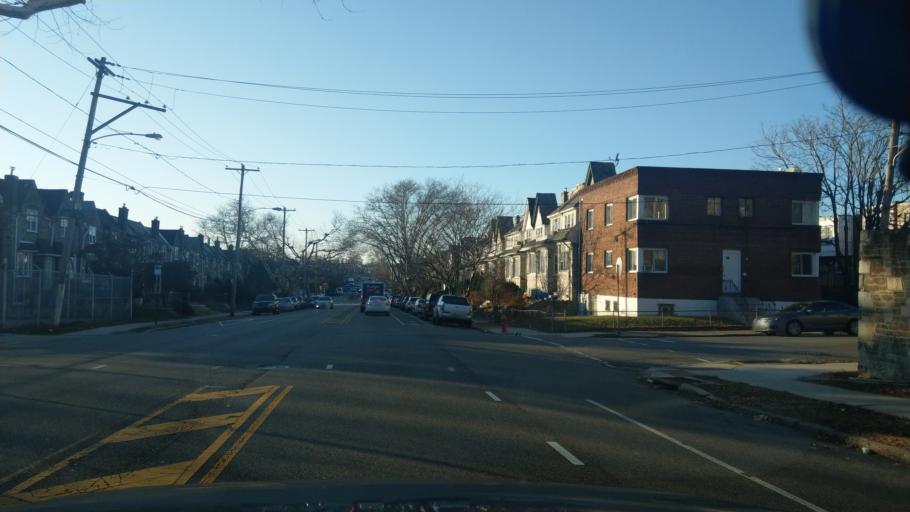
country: US
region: Pennsylvania
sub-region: Montgomery County
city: Wyncote
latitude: 40.0538
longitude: -75.1429
